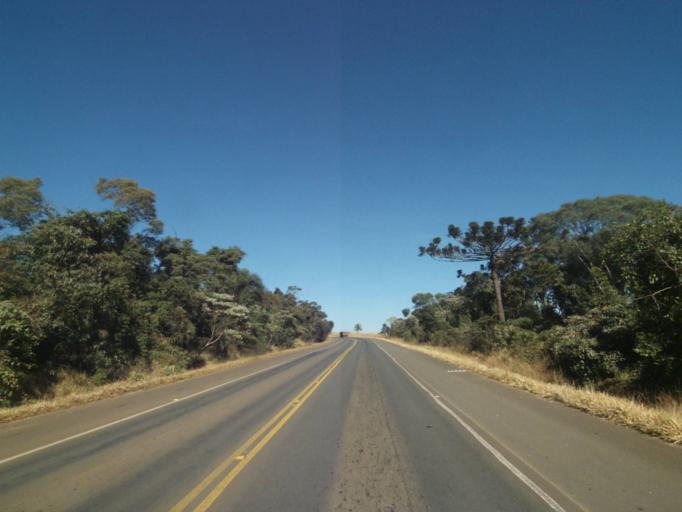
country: BR
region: Parana
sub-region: Tibagi
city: Tibagi
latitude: -24.6661
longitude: -50.4523
